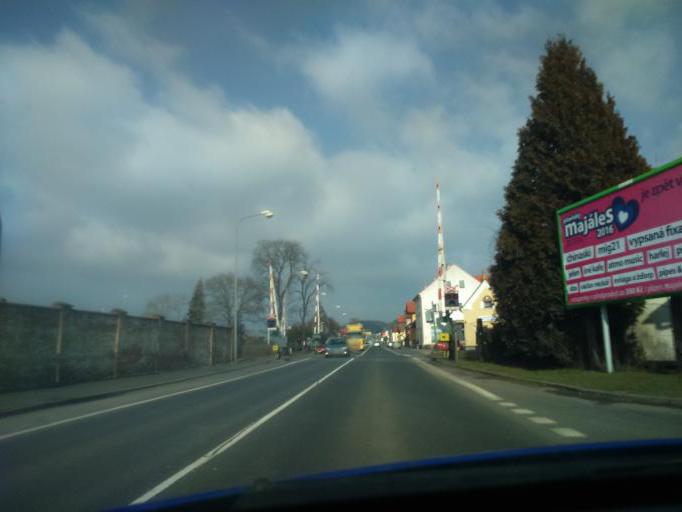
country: CZ
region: Plzensky
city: Holysov
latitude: 49.5941
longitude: 13.1004
